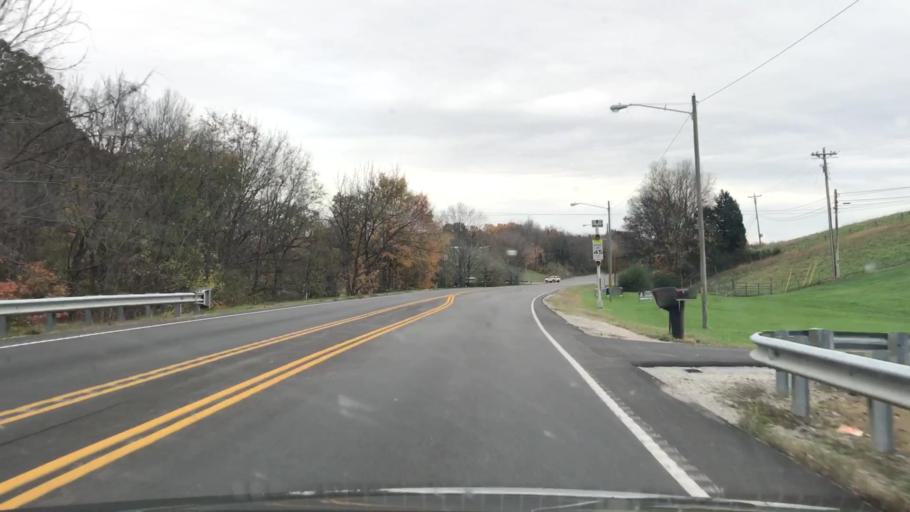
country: US
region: Kentucky
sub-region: Barren County
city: Glasgow
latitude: 37.0243
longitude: -85.9061
